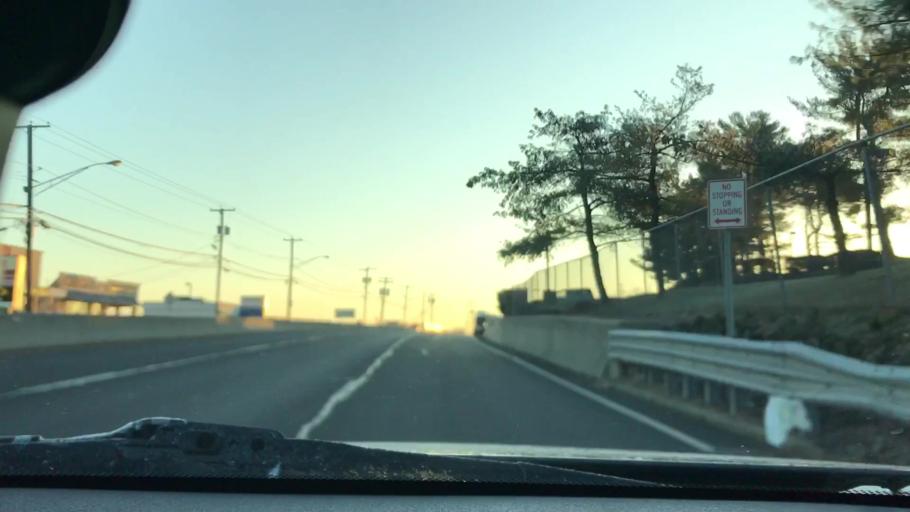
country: US
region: New Jersey
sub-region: Morris County
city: Florham Park
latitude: 40.8123
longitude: -74.3910
